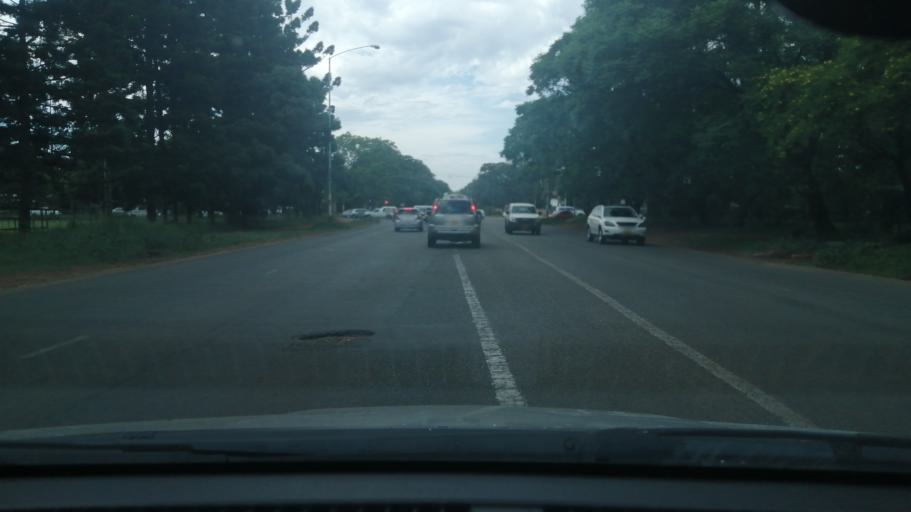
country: ZW
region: Harare
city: Harare
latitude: -17.8209
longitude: 31.0313
